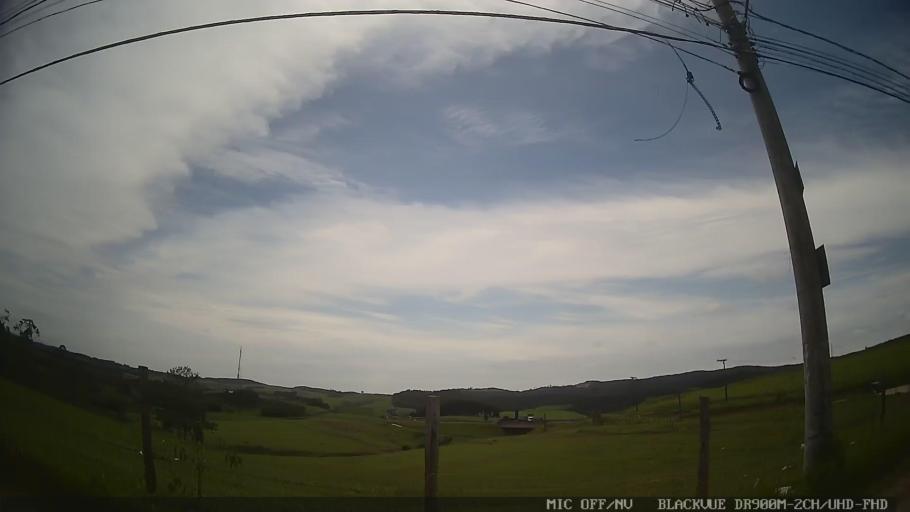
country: BR
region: Sao Paulo
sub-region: Santa Isabel
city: Santa Isabel
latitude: -23.3910
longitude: -46.1715
